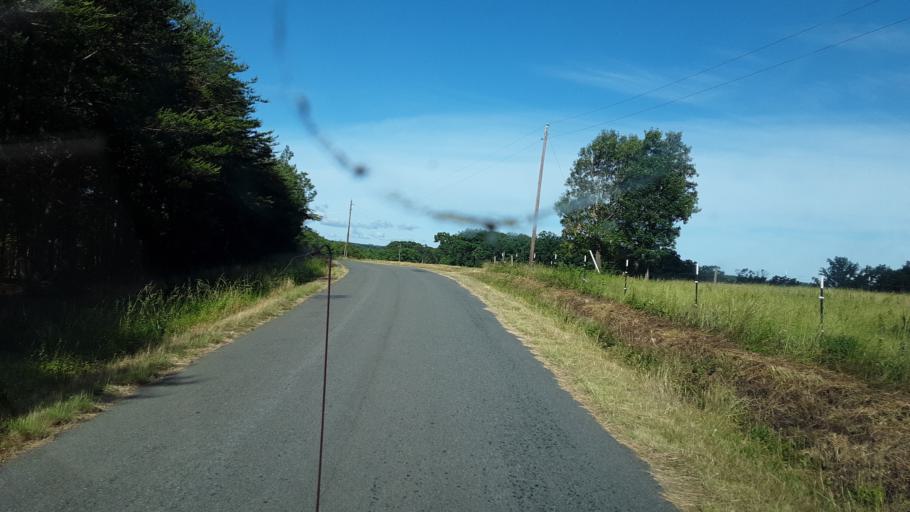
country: US
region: Virginia
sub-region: Pittsylvania County
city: Chatham
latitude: 36.8400
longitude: -79.4012
